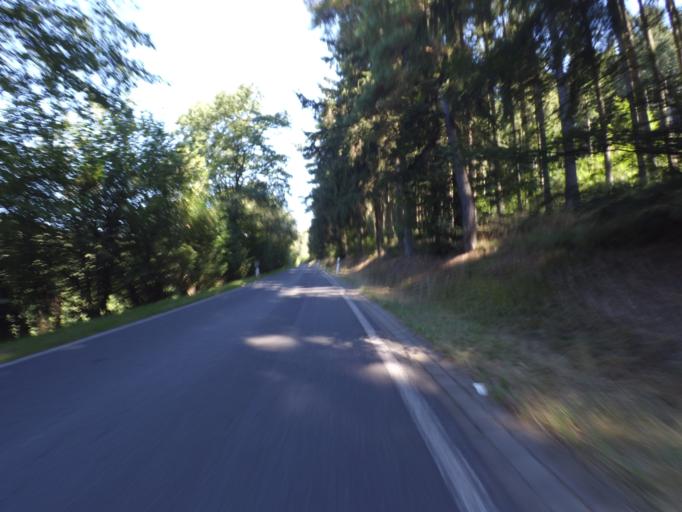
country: DE
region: Rheinland-Pfalz
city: Wagenhausen
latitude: 50.1517
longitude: 6.9737
